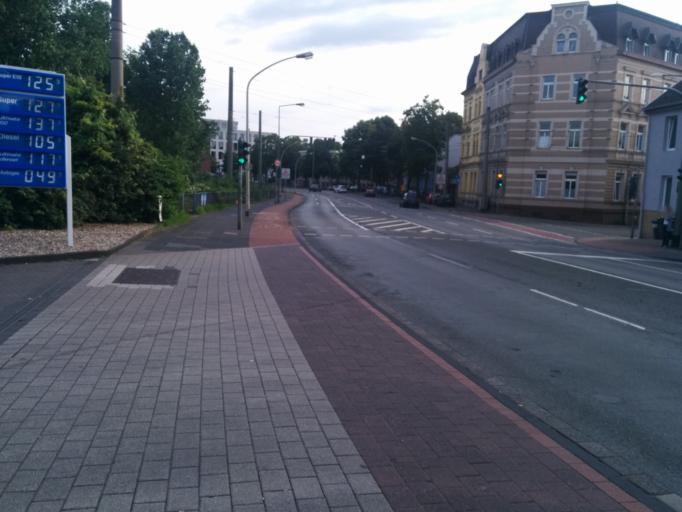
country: DE
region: North Rhine-Westphalia
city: Meiderich
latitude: 51.4530
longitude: 6.7398
